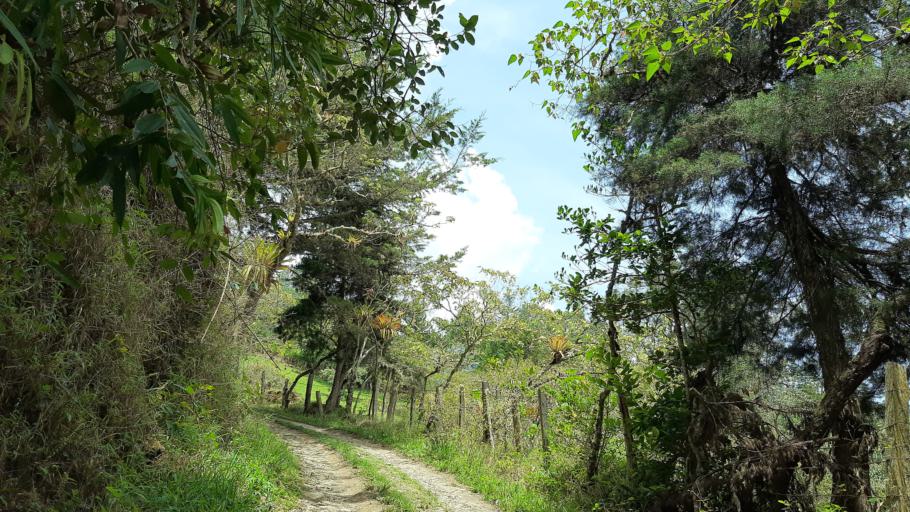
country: CO
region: Boyaca
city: Garagoa
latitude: 5.0623
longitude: -73.3595
